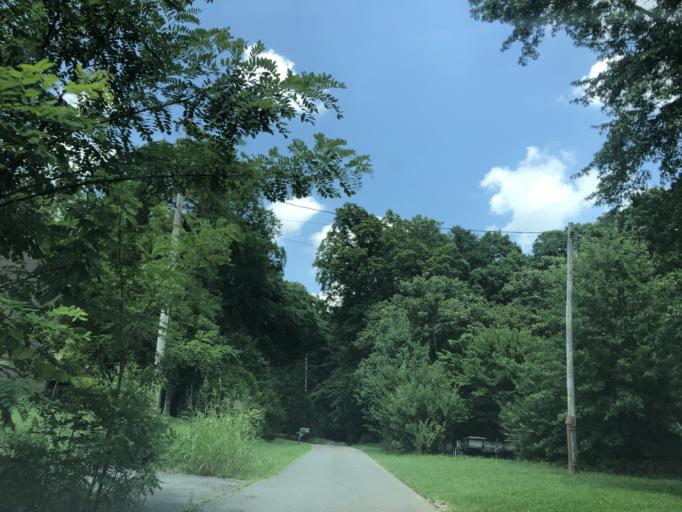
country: US
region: Tennessee
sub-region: Williamson County
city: Brentwood Estates
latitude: 36.0262
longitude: -86.7252
